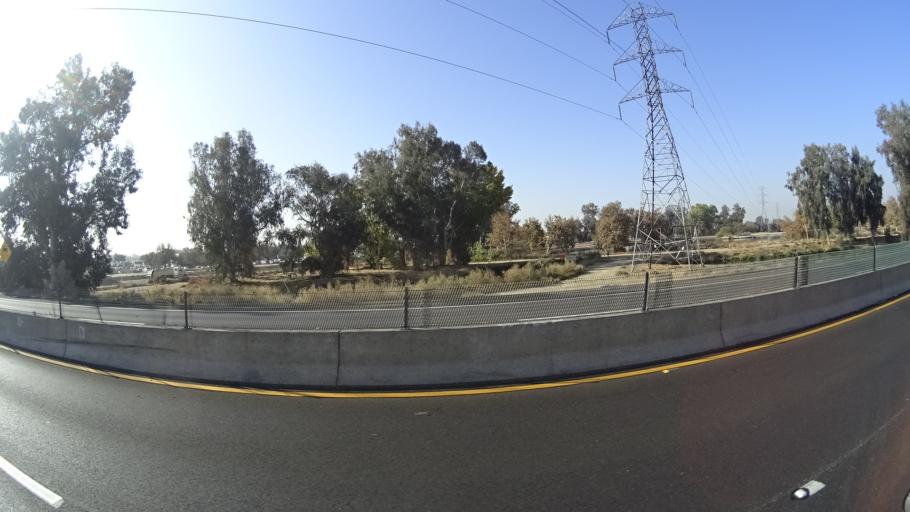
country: US
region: California
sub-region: Kern County
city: Oildale
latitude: 35.3977
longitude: -119.0337
